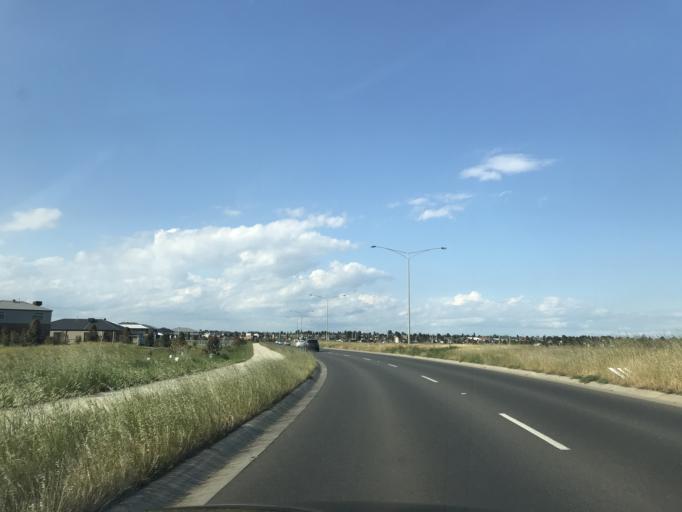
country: AU
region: Victoria
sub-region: Wyndham
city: Hoppers Crossing
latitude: -37.8981
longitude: 144.7113
